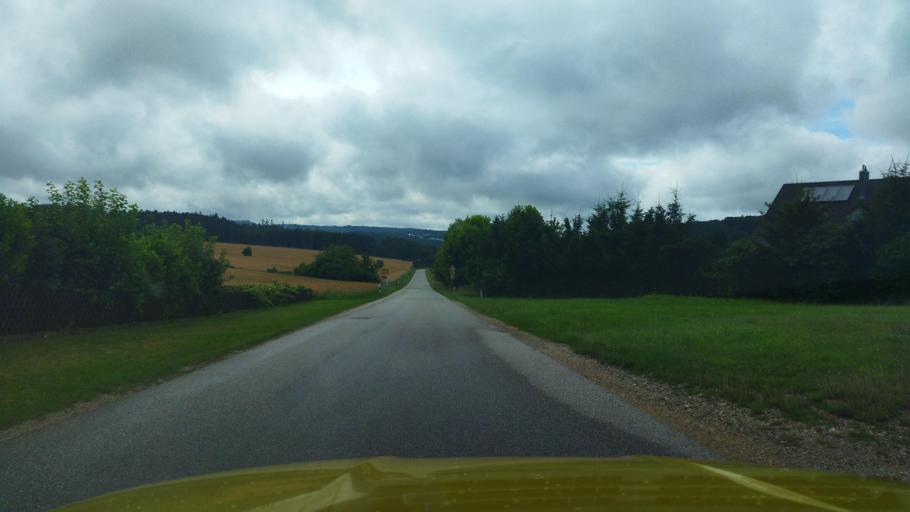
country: DE
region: Bavaria
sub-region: Lower Bavaria
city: Riedenburg
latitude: 48.9425
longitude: 11.7063
